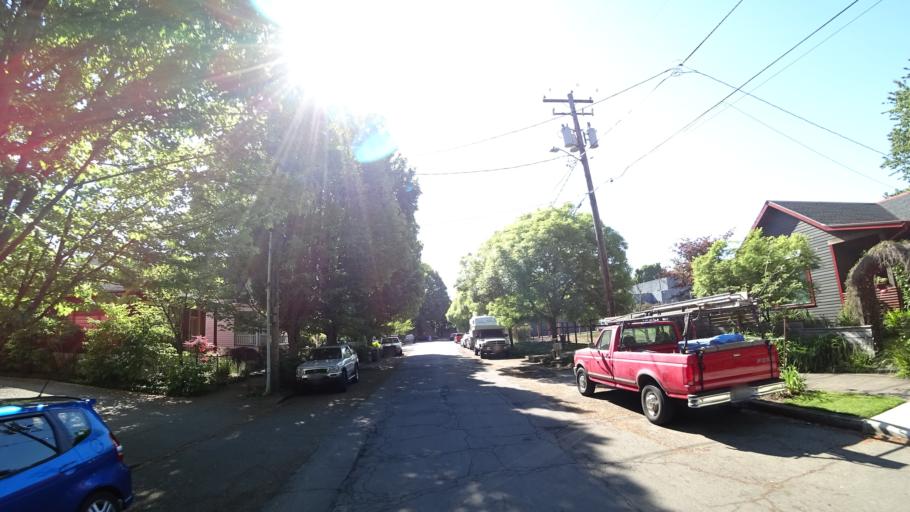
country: US
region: Oregon
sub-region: Multnomah County
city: Portland
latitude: 45.5404
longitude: -122.6604
